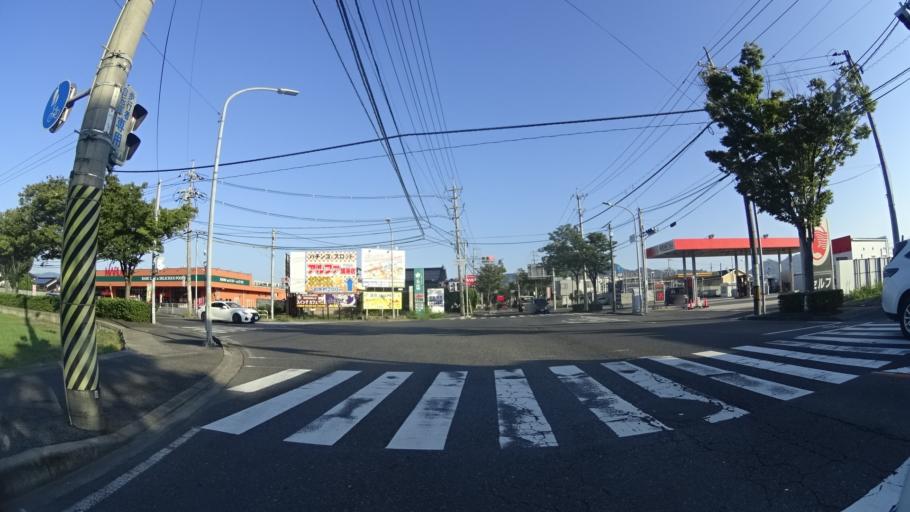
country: JP
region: Shimane
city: Sakaiminato
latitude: 35.5221
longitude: 133.2134
